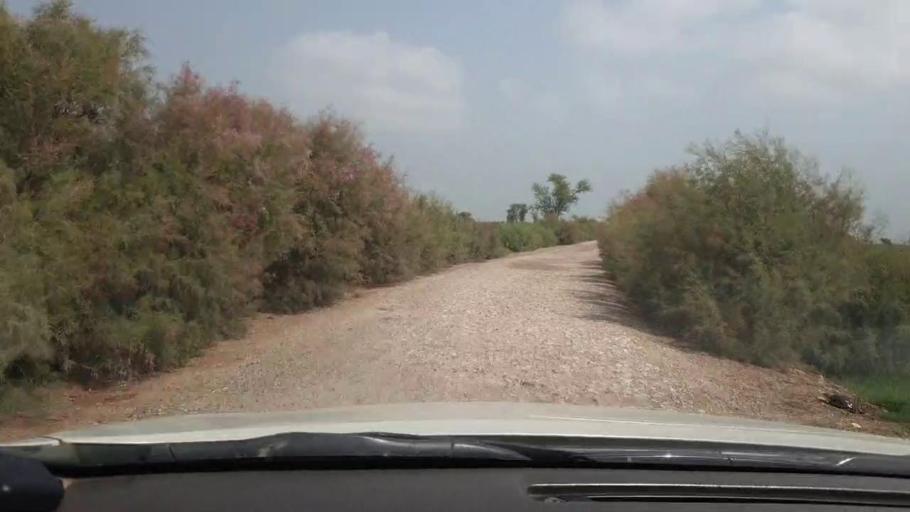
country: PK
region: Sindh
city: Garhi Yasin
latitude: 28.0073
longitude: 68.5396
